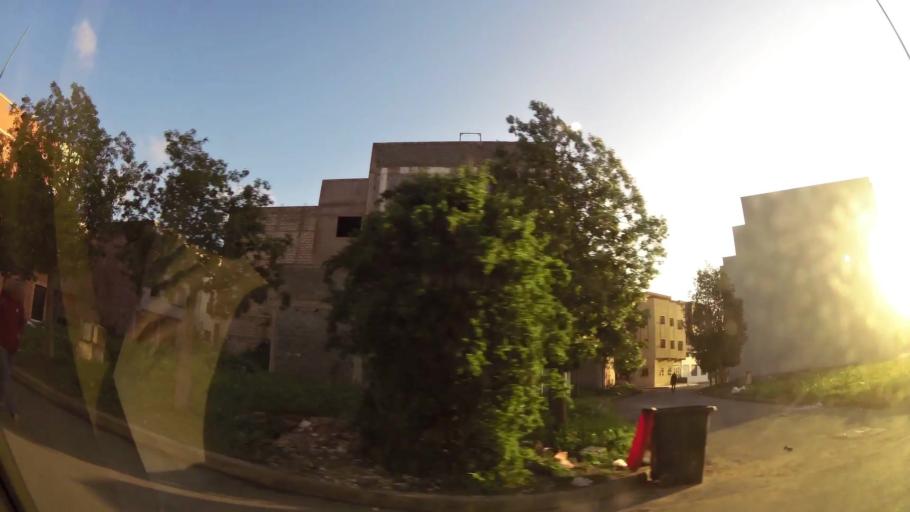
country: MA
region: Chaouia-Ouardigha
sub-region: Settat Province
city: Settat
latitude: 32.9908
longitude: -7.6045
